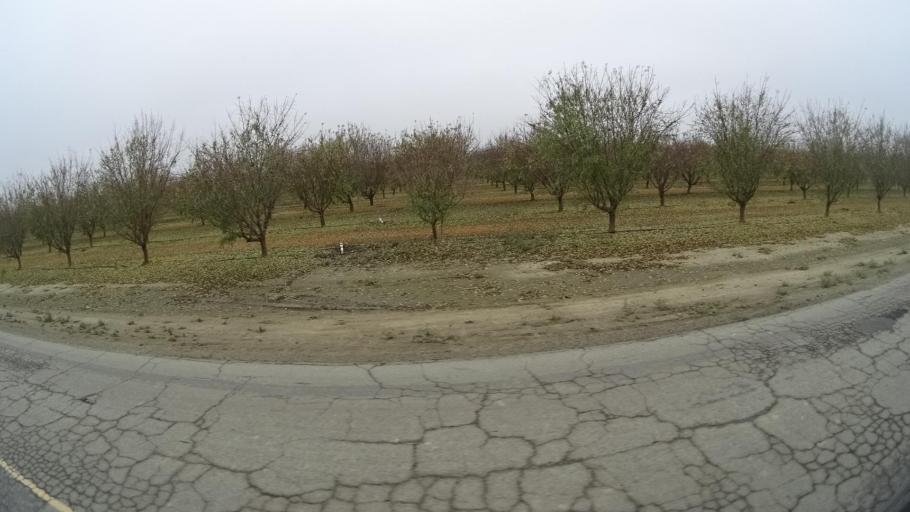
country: US
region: California
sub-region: Kern County
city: Wasco
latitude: 35.7057
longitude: -119.4016
